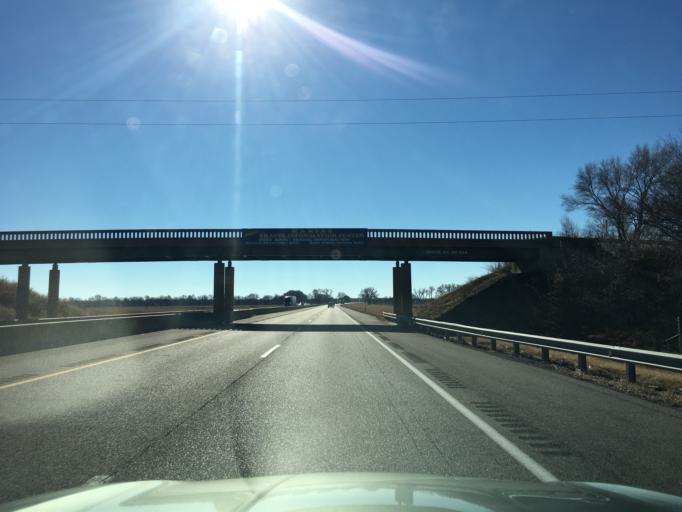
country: US
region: Kansas
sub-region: Sumner County
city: Belle Plaine
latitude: 37.4218
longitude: -97.3213
